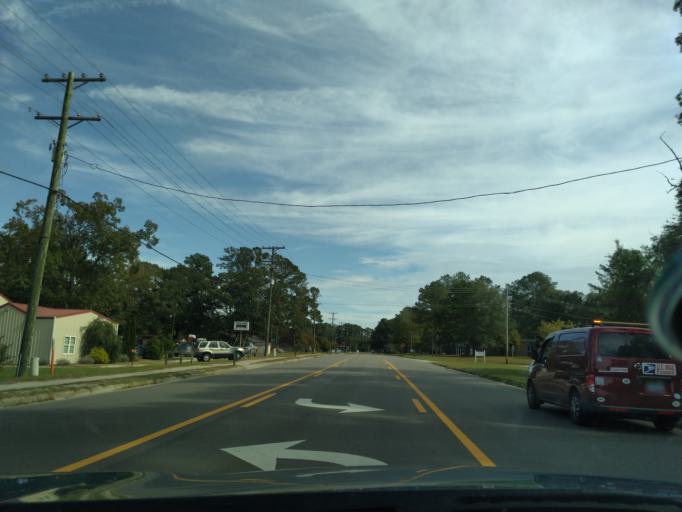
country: US
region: North Carolina
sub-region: Beaufort County
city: River Road
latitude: 35.5053
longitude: -76.9912
